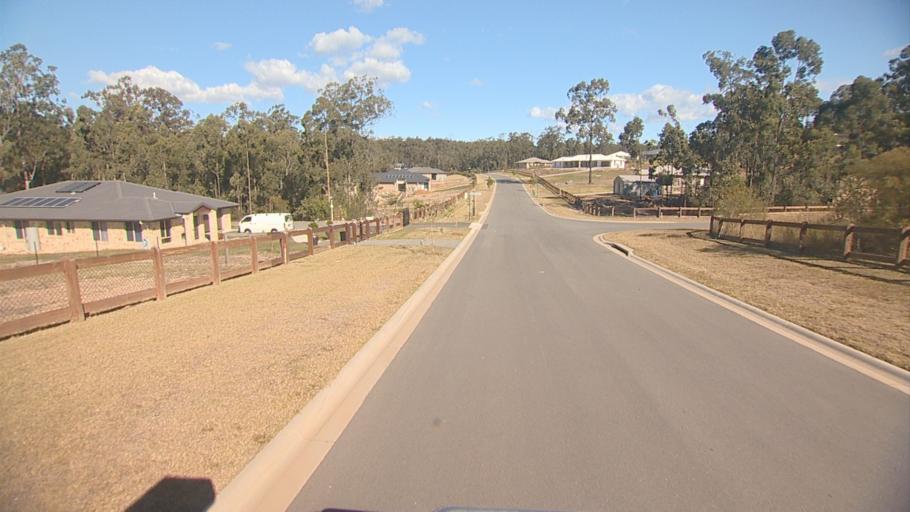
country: AU
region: Queensland
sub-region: Ipswich
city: Springfield Lakes
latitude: -27.7310
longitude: 152.9069
